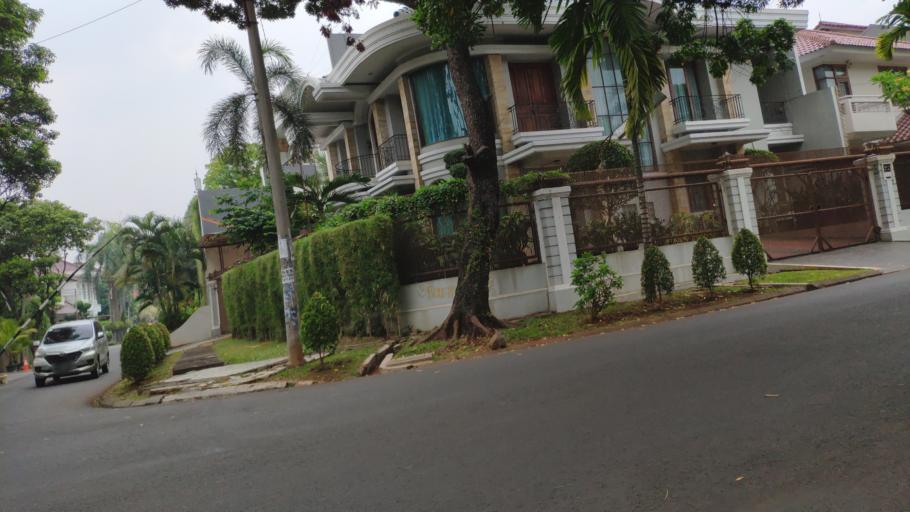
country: ID
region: Banten
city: South Tangerang
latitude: -6.2668
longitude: 106.7785
